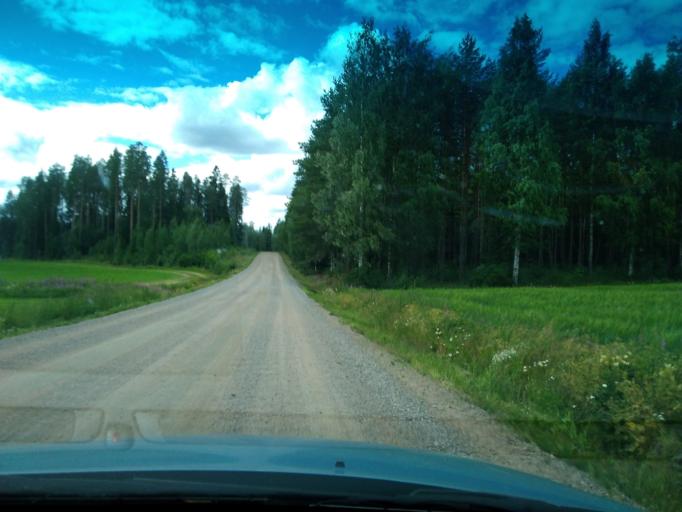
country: FI
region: Central Finland
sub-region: Saarijaervi-Viitasaari
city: Karstula
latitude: 62.7918
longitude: 24.9835
